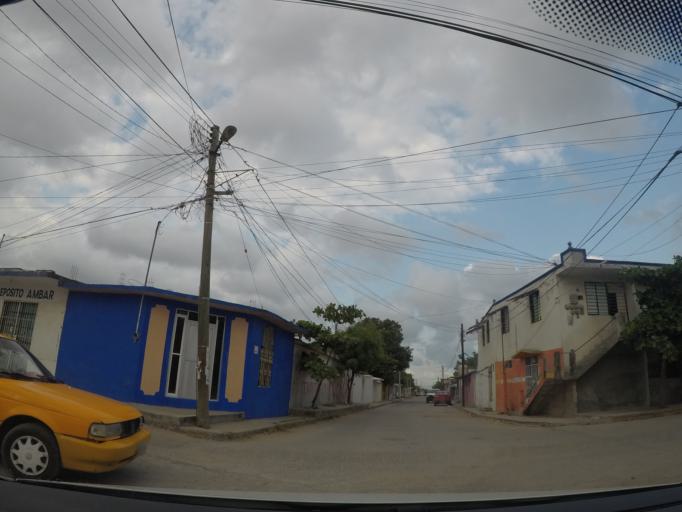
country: MX
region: Oaxaca
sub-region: Salina Cruz
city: Salina Cruz
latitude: 16.2138
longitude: -95.1988
